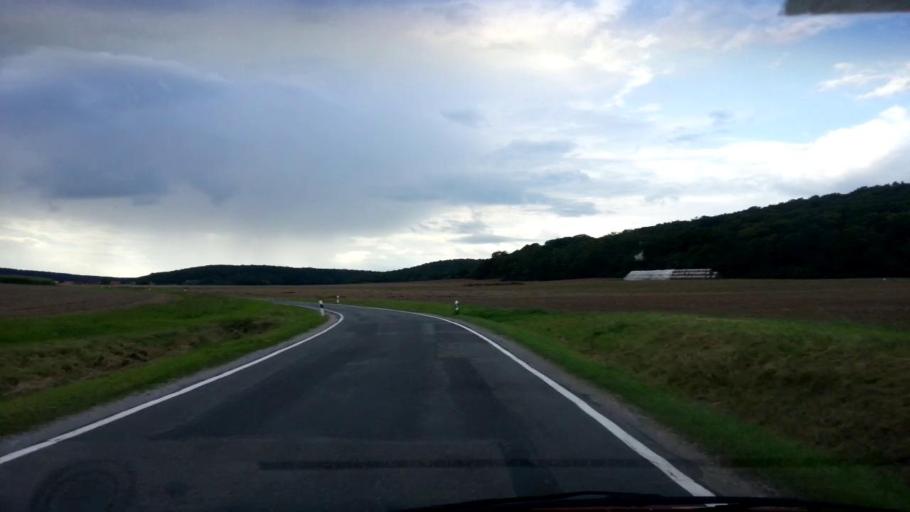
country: DE
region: Bavaria
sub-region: Regierungsbezirk Mittelfranken
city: Markt Taschendorf
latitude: 49.7438
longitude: 10.5522
